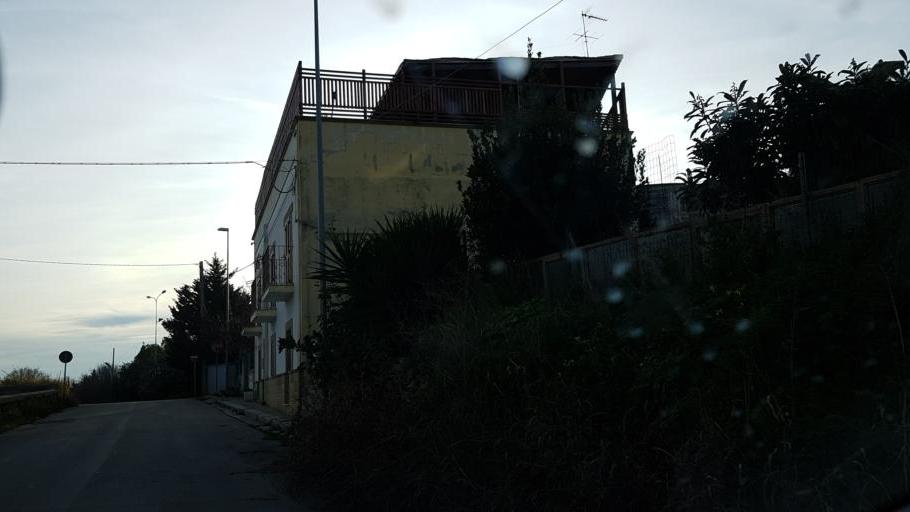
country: IT
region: Apulia
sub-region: Provincia di Brindisi
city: Brindisi
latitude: 40.6329
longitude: 17.9505
